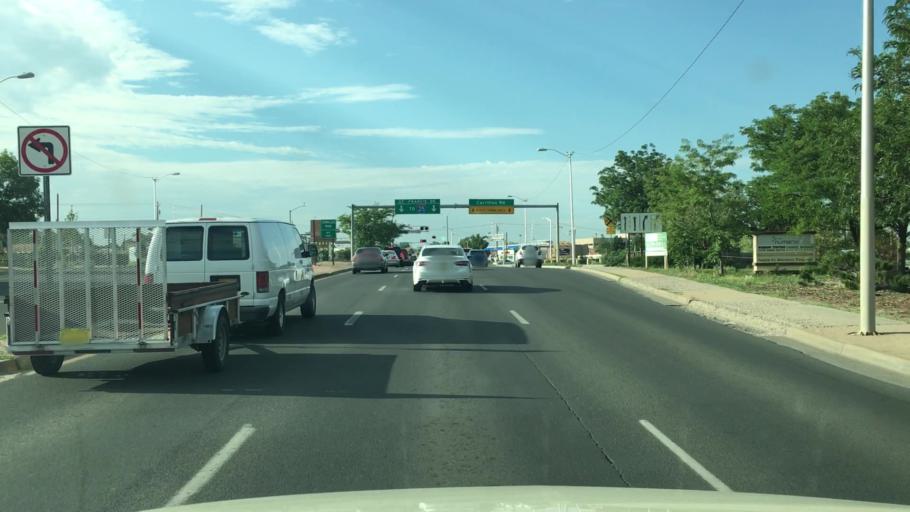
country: US
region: New Mexico
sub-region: Santa Fe County
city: Santa Fe
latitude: 35.6791
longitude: -105.9543
